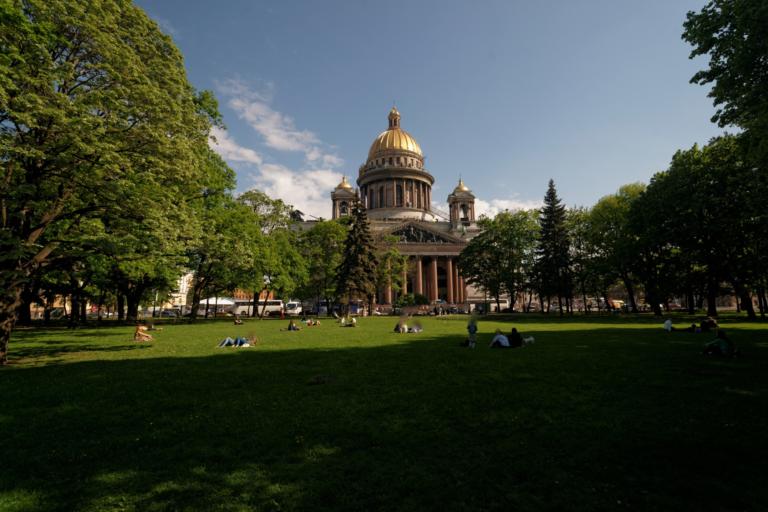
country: RU
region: St.-Petersburg
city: Saint Petersburg
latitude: 59.9354
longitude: 30.3047
